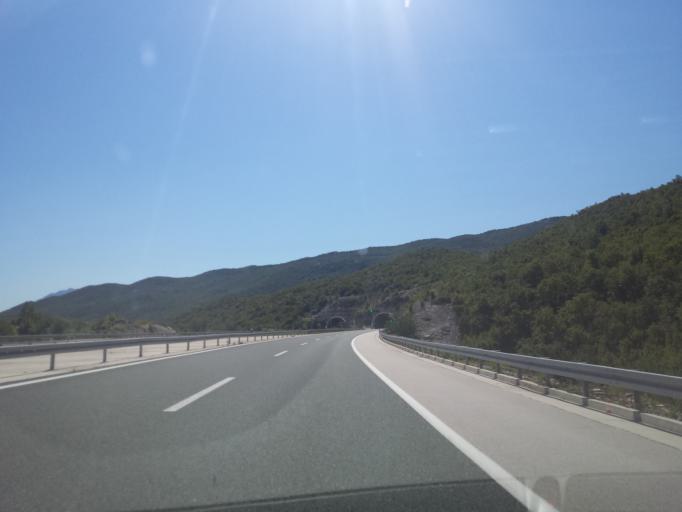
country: HR
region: Splitsko-Dalmatinska
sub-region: Grad Omis
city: Omis
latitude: 43.4885
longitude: 16.7993
